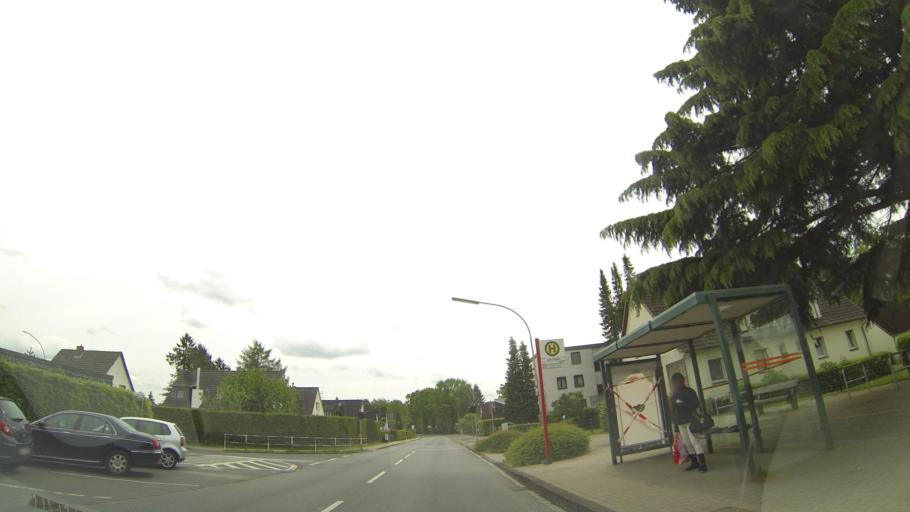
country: DE
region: Schleswig-Holstein
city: Halstenbek
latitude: 53.6049
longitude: 9.8434
